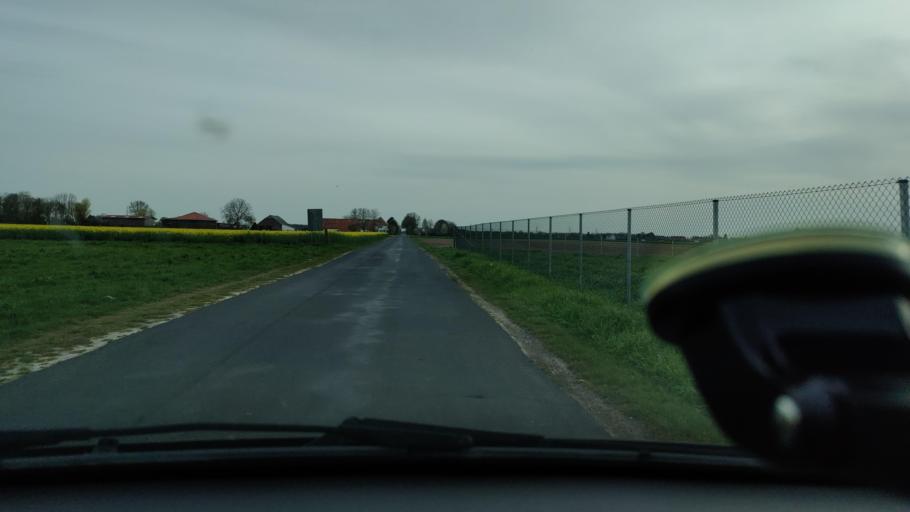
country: DE
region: North Rhine-Westphalia
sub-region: Regierungsbezirk Dusseldorf
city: Goch
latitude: 51.7102
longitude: 6.1822
